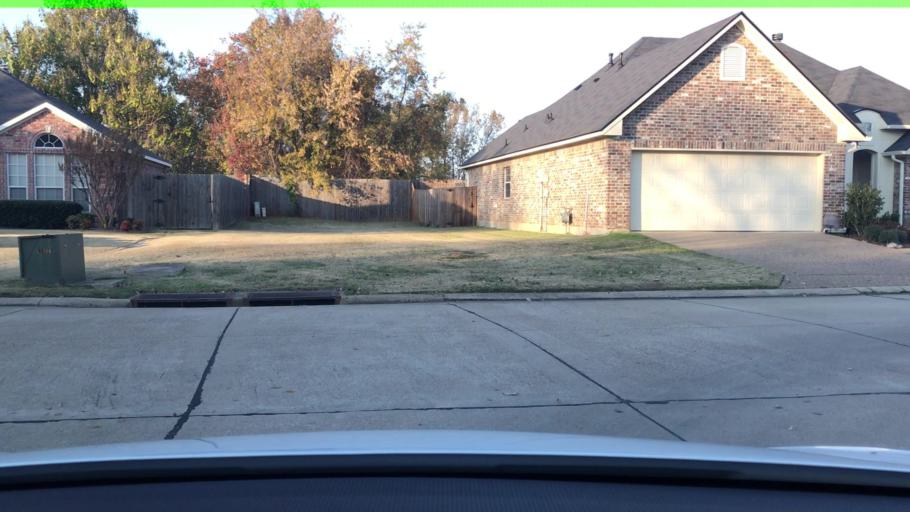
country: US
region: Louisiana
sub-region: Bossier Parish
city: Bossier City
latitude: 32.4078
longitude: -93.7004
